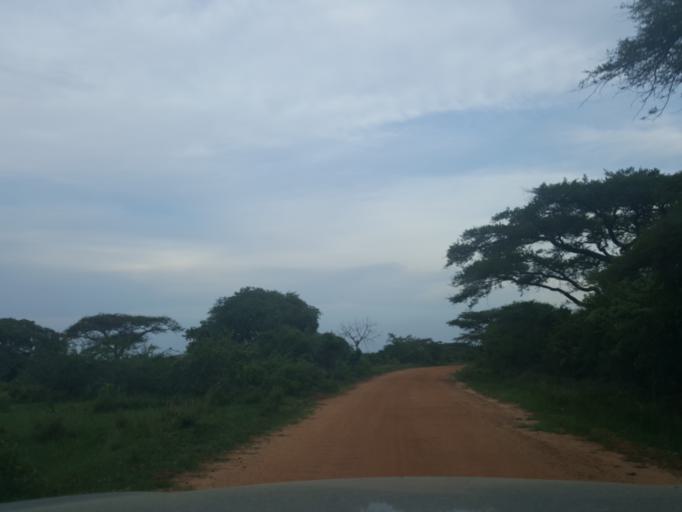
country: ZA
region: Limpopo
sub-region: Mopani District Municipality
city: Hoedspruit
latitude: -24.5882
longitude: 30.9520
